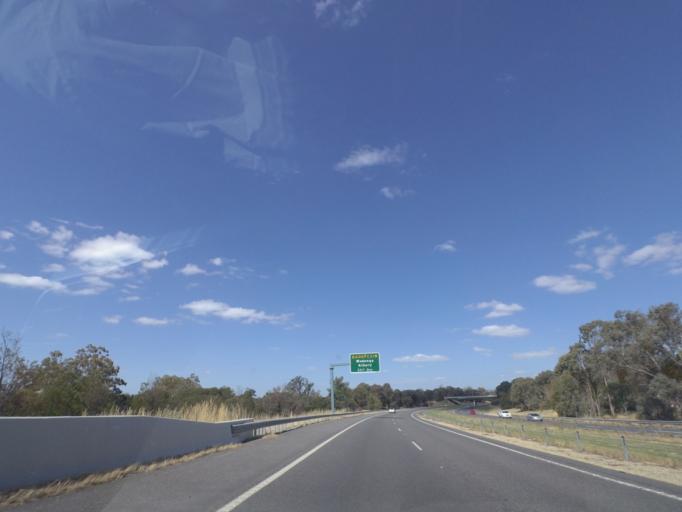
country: AU
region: Victoria
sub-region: Wodonga
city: Wodonga
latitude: -36.1071
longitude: 146.8654
